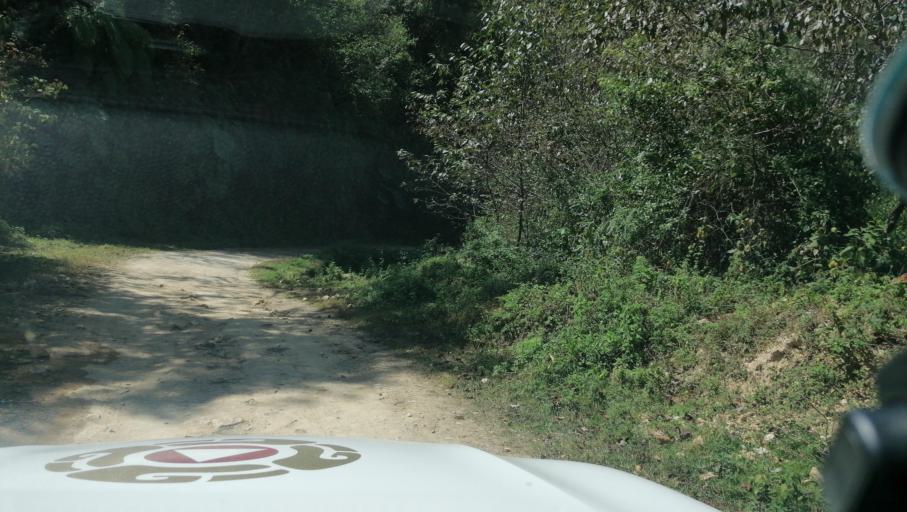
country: GT
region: San Marcos
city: Tacana
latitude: 15.2063
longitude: -92.2083
